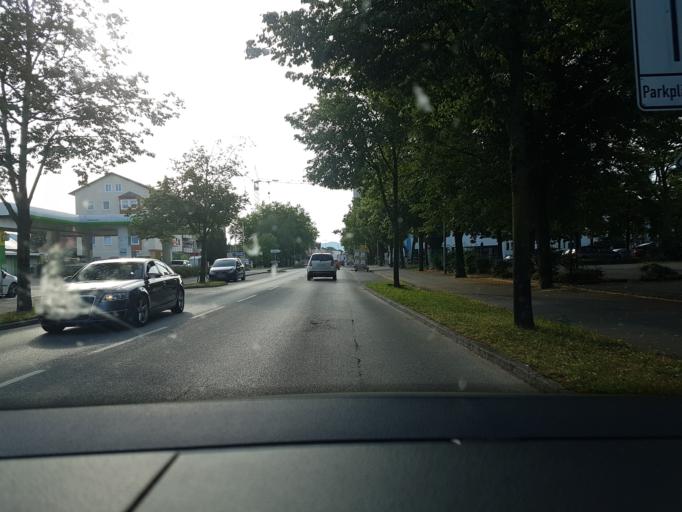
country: DE
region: Bavaria
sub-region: Upper Bavaria
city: Freilassing
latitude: 47.8422
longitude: 12.9758
